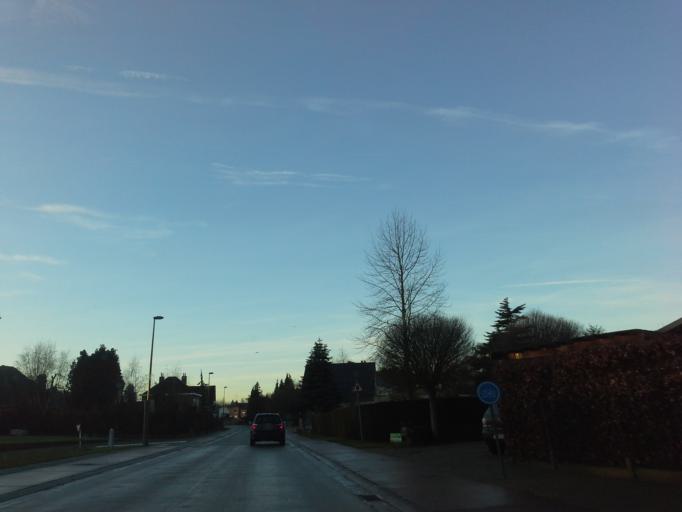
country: BE
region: Flanders
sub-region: Provincie Vlaams-Brabant
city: Bekkevoort
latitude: 50.9438
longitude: 4.9562
